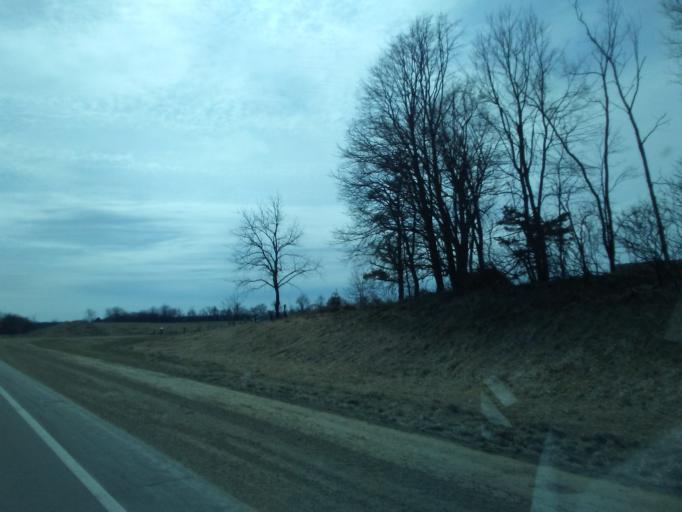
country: US
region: Iowa
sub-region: Winneshiek County
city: Decorah
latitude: 43.3492
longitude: -91.8055
